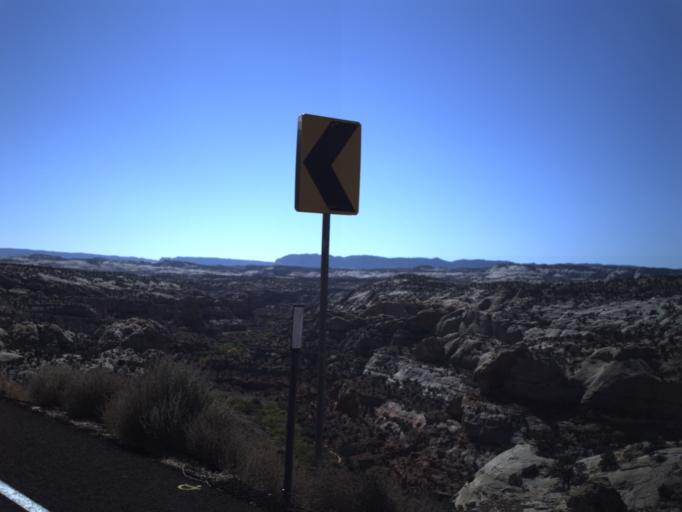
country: US
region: Utah
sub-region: Wayne County
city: Loa
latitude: 37.8133
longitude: -111.4087
